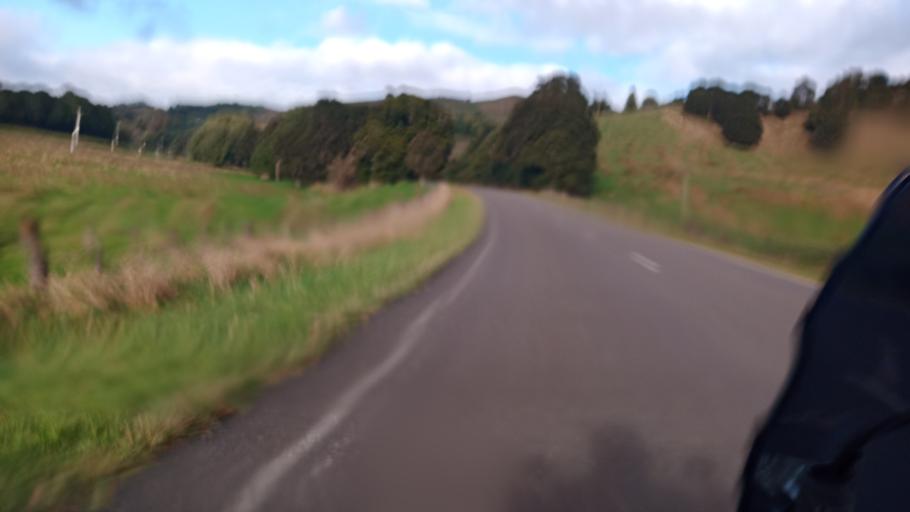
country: NZ
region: Gisborne
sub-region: Gisborne District
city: Gisborne
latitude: -38.5909
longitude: 177.7793
